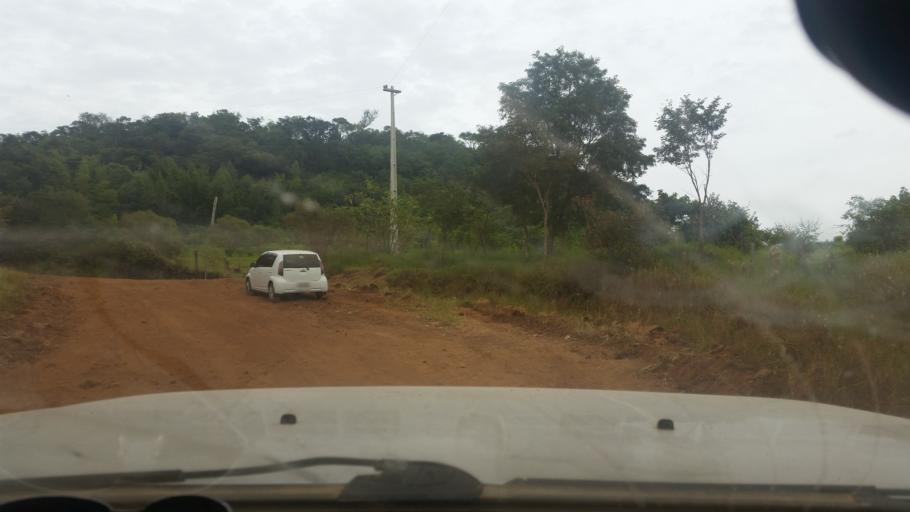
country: PY
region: Guaira
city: Independencia
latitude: -25.8049
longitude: -56.2723
